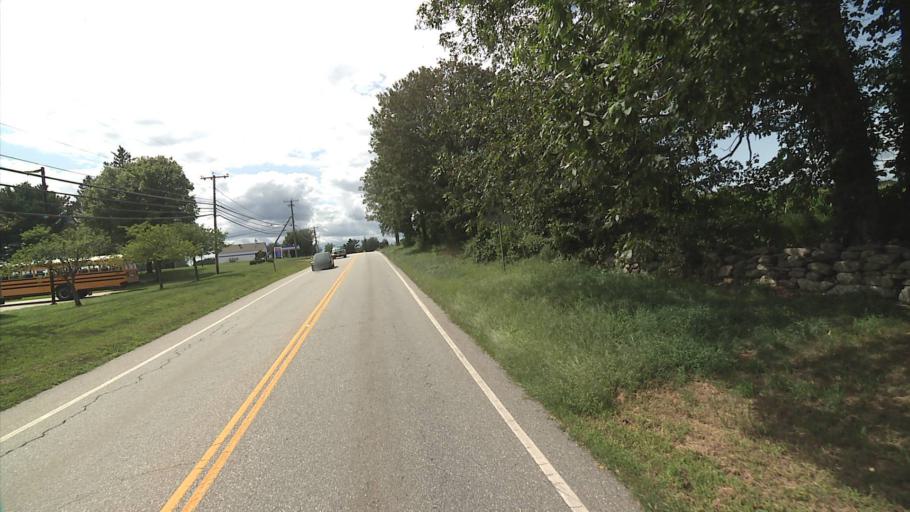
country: US
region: Connecticut
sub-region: Windham County
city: South Windham
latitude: 41.6267
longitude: -72.2379
